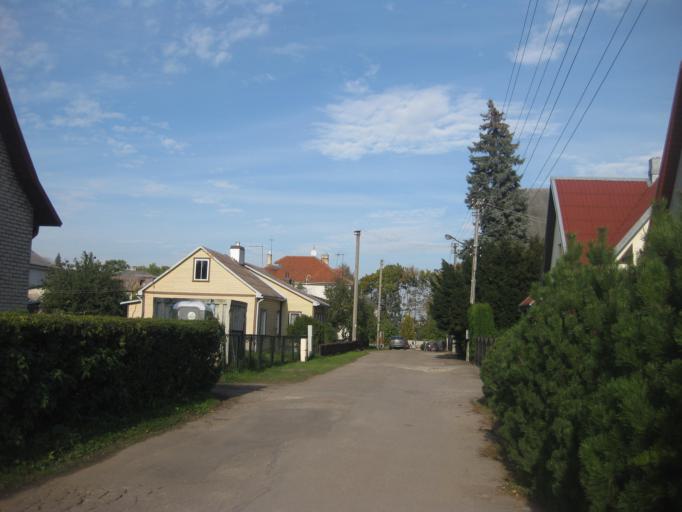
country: LT
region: Kauno apskritis
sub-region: Kaunas
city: Aleksotas
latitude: 54.8884
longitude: 23.8927
